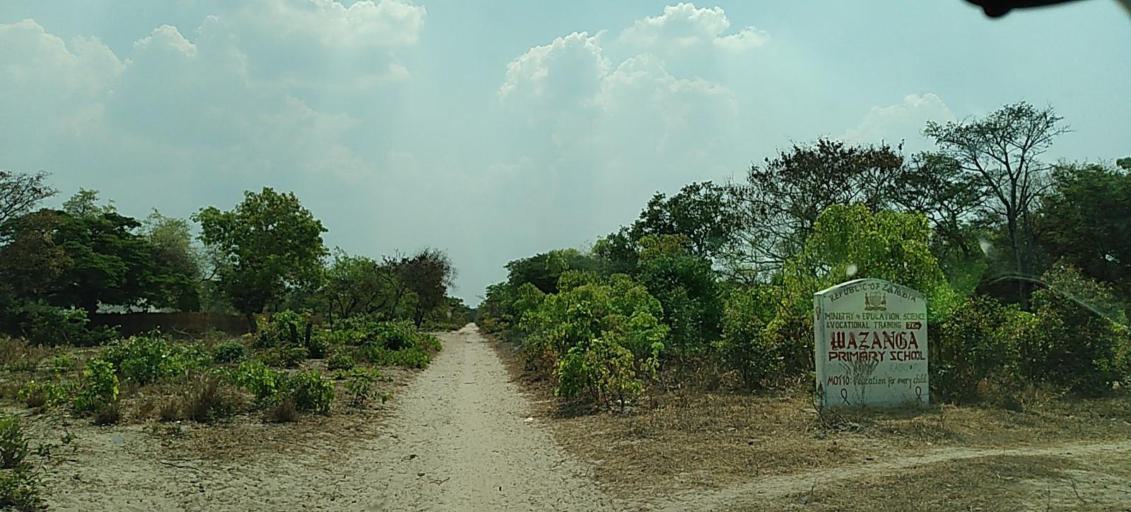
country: ZM
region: North-Western
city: Kabompo
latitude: -13.4012
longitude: 23.8169
